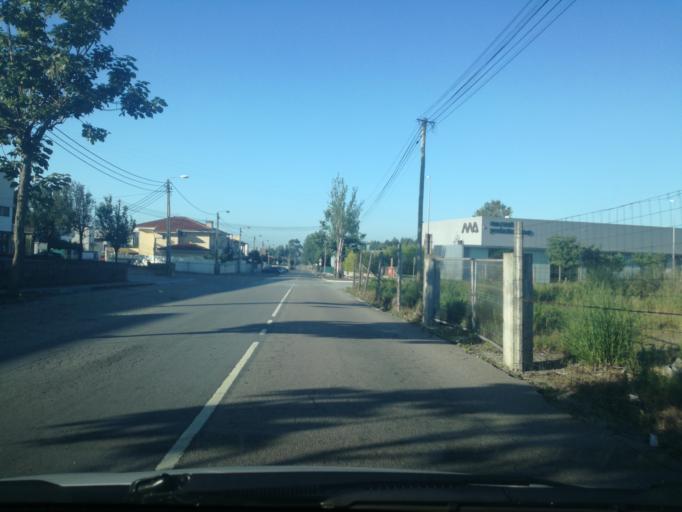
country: PT
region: Porto
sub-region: Maia
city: Milheiros
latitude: 41.2240
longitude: -8.5850
